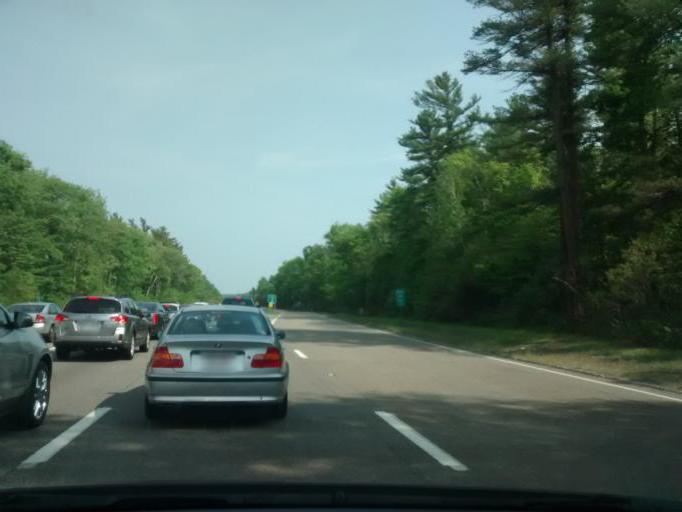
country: US
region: Massachusetts
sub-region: Bristol County
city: Raynham Center
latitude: 41.9353
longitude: -71.0112
